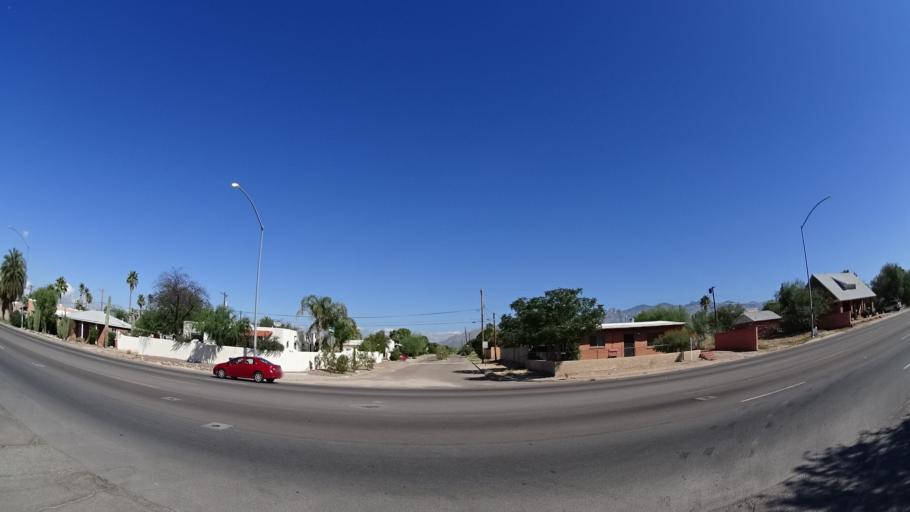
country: US
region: Arizona
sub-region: Pima County
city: Tucson
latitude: 32.2497
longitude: -110.9498
